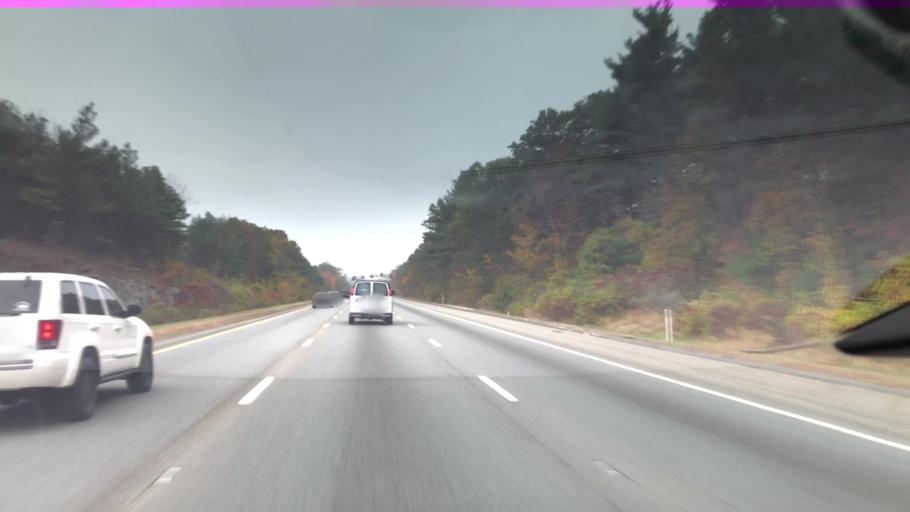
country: US
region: Massachusetts
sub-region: Worcester County
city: Harvard
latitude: 42.4584
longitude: -71.5728
